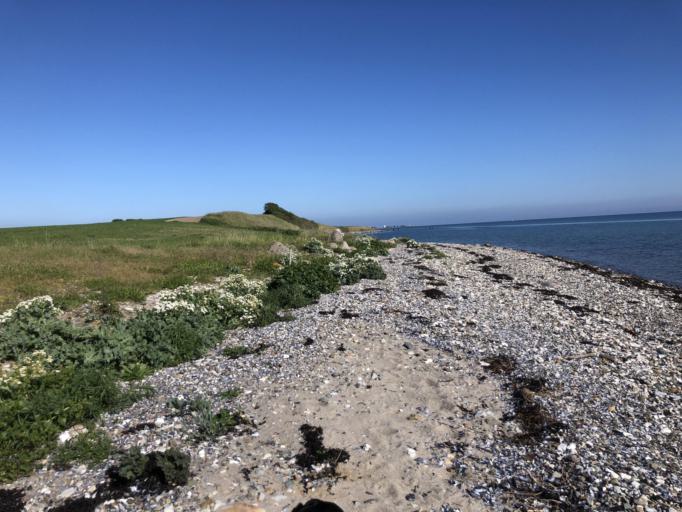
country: DK
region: Zealand
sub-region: Slagelse Kommune
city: Skaelskor
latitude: 55.1978
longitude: 11.1765
